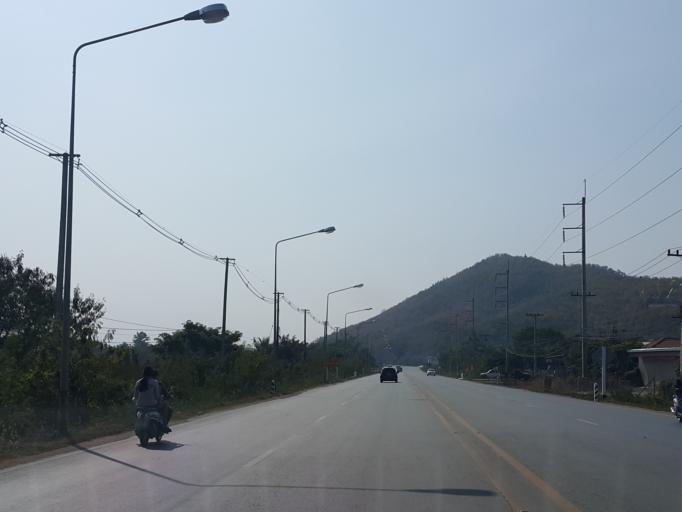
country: TH
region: Chiang Mai
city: Chom Thong
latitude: 18.3927
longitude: 98.6788
